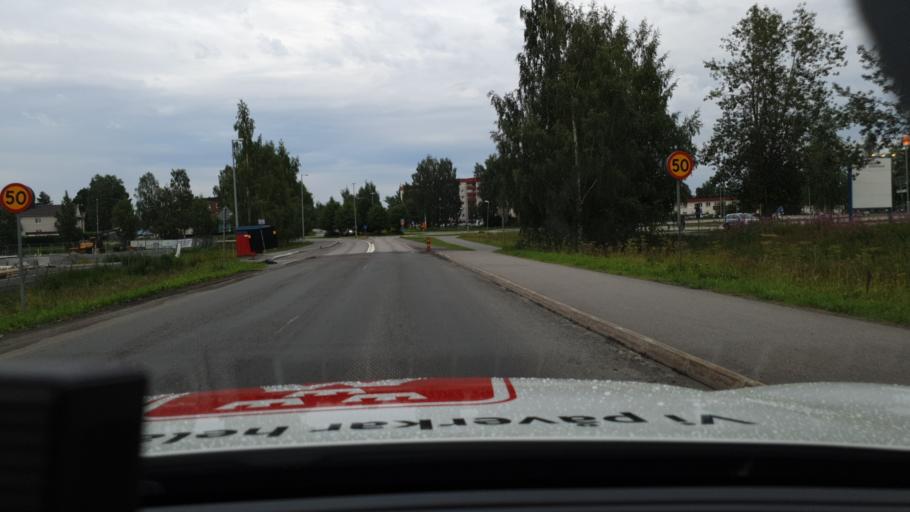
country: SE
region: Norrbotten
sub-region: Bodens Kommun
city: Boden
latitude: 65.8241
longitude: 21.6651
